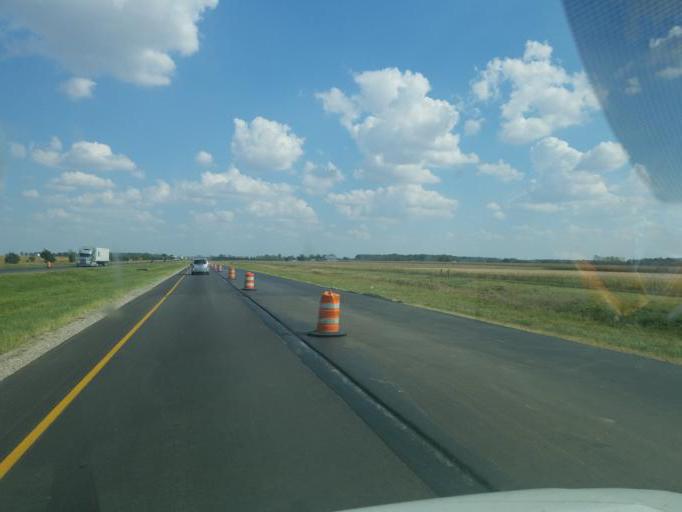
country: US
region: Ohio
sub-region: Van Wert County
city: Van Wert
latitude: 40.8697
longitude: -84.4981
